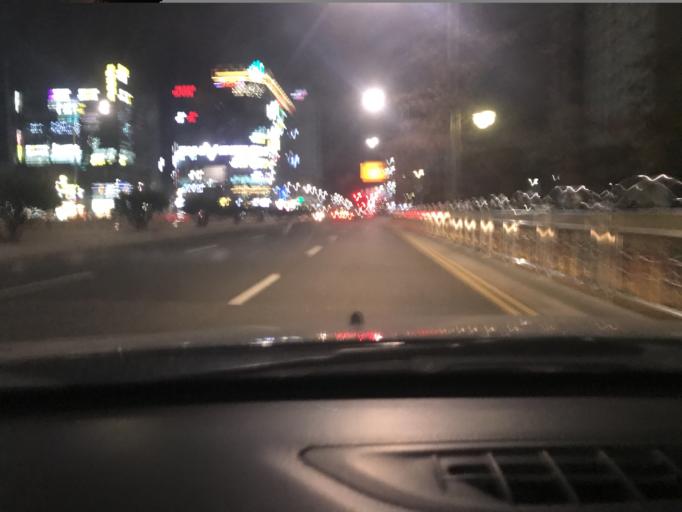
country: KR
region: Daegu
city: Hwawon
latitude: 35.6952
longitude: 128.4577
